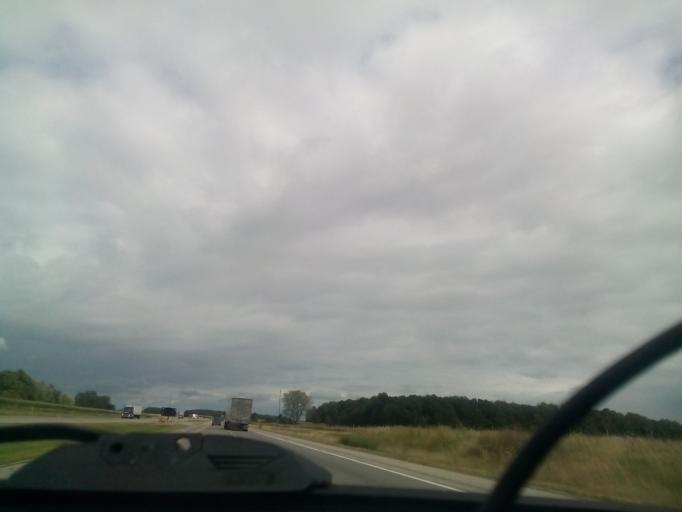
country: US
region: Ohio
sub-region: Williams County
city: Montpelier
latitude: 41.6170
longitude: -84.6523
